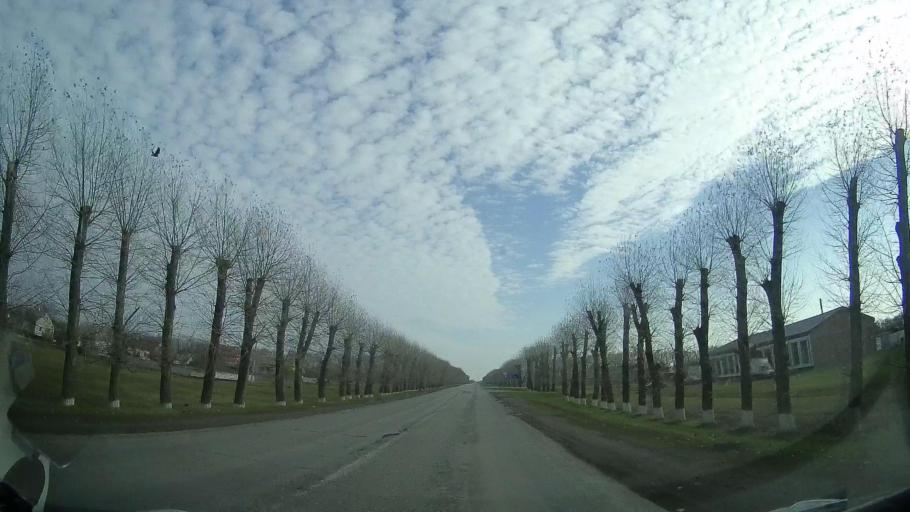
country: RU
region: Rostov
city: Tselina
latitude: 46.5283
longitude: 41.0556
